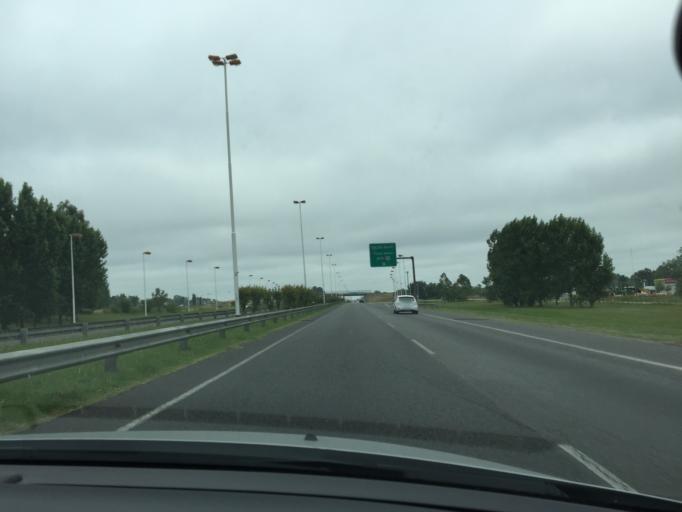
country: AR
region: Buenos Aires
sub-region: Partido de Ezeiza
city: Ezeiza
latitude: -34.8730
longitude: -58.5829
